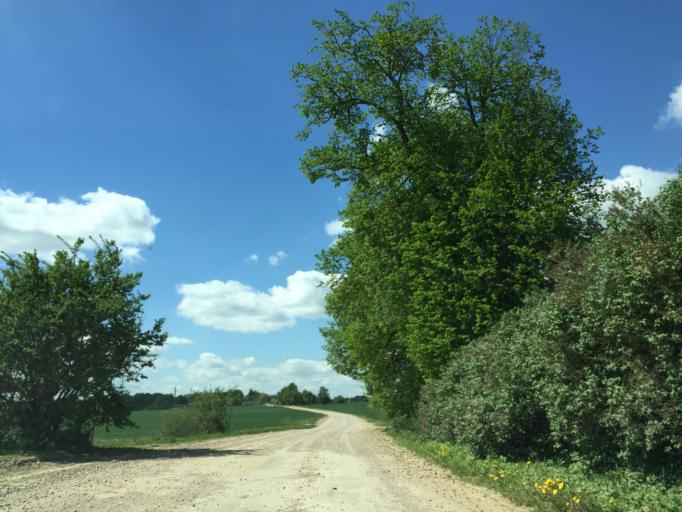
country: LV
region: Bauskas Rajons
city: Bauska
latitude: 56.4972
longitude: 24.1419
